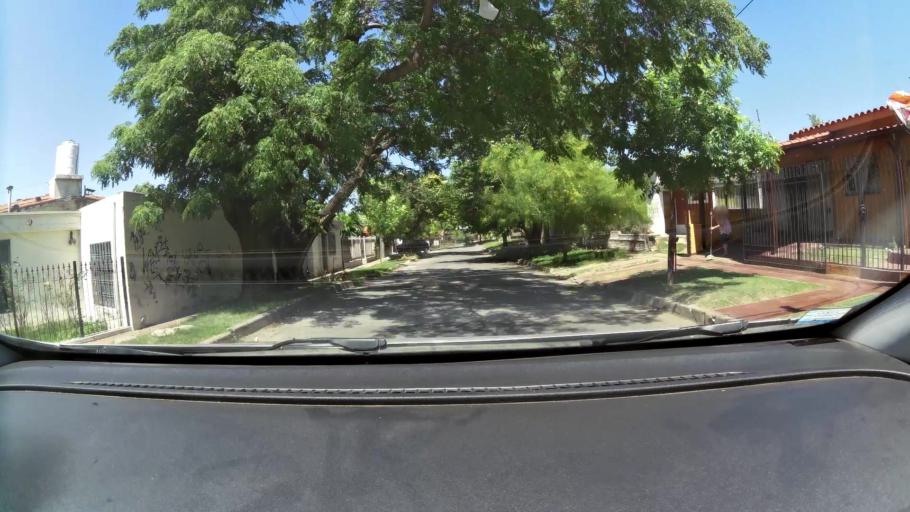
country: AR
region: Cordoba
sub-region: Departamento de Capital
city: Cordoba
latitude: -31.4309
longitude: -64.2108
